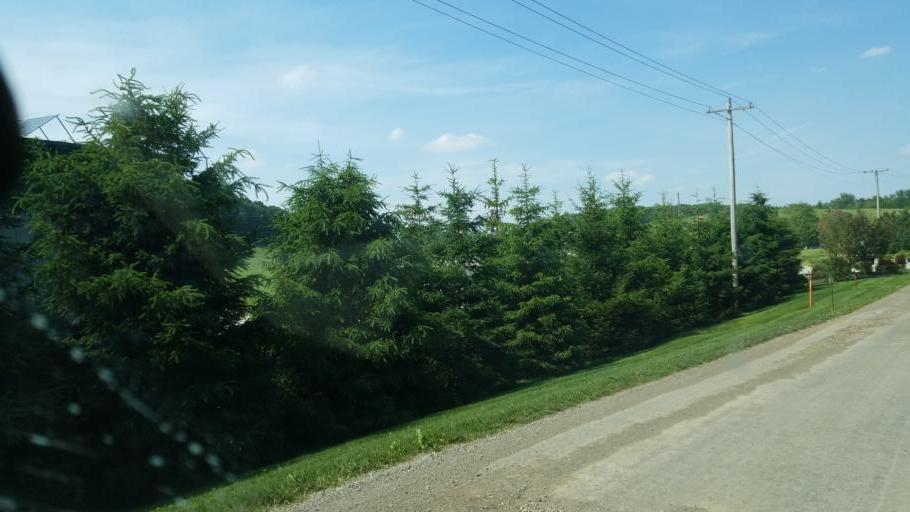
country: US
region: Ohio
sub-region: Knox County
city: Danville
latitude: 40.5509
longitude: -82.3214
